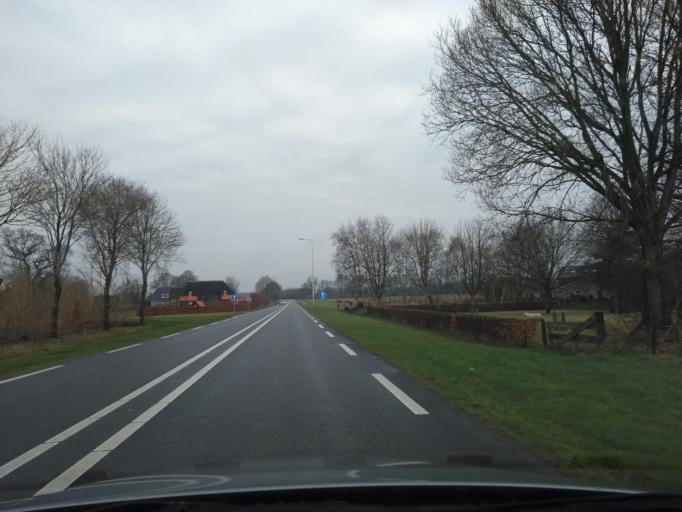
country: NL
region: Overijssel
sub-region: Gemeente Steenwijkerland
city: Sint Jansklooster
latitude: 52.6568
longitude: 6.0070
